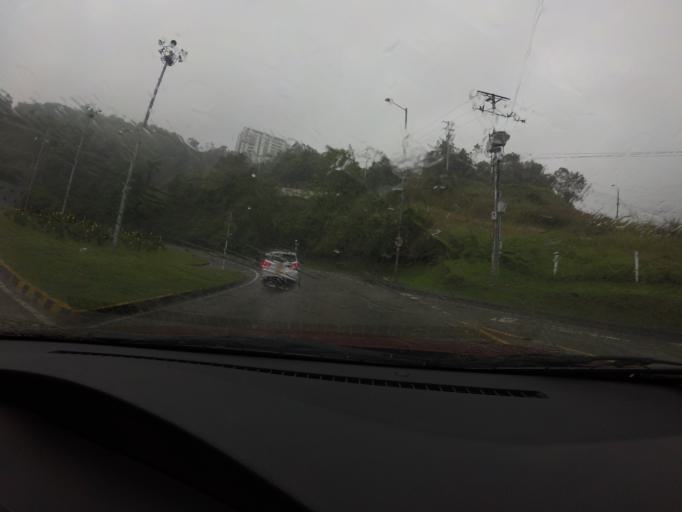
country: CO
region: Caldas
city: Villamaria
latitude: 5.0425
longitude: -75.4790
